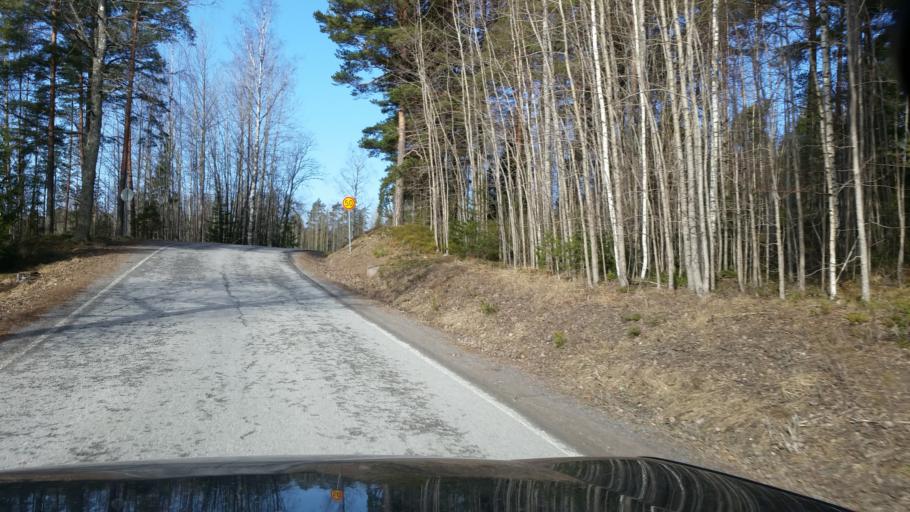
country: FI
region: Uusimaa
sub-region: Raaseporin
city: Inga
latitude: 60.0510
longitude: 24.0439
